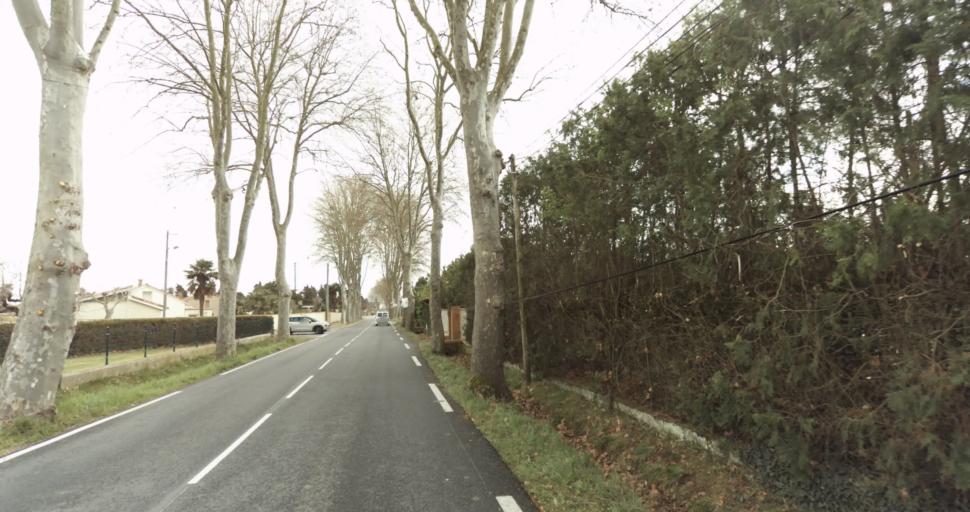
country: FR
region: Midi-Pyrenees
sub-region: Departement de la Haute-Garonne
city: Auterive
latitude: 43.3504
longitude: 1.4591
